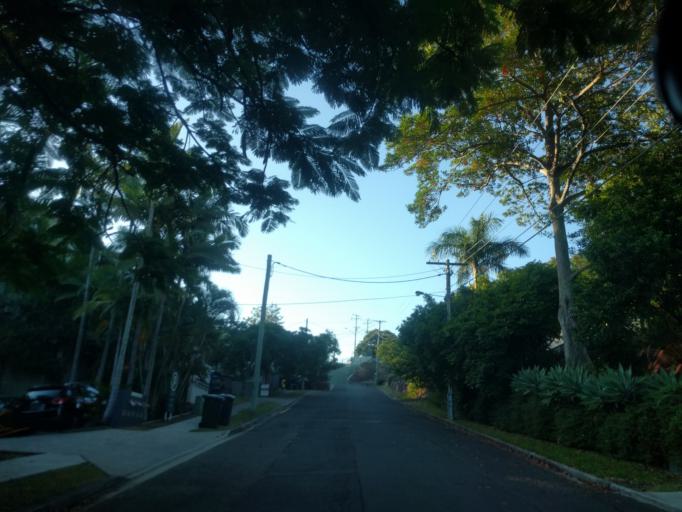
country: AU
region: Queensland
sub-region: Brisbane
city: Wilston
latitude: -27.4468
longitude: 153.0154
